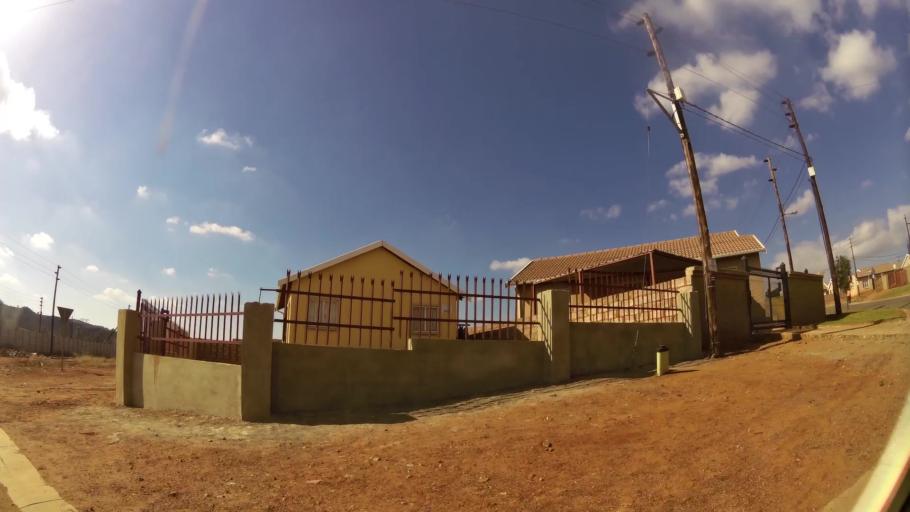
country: ZA
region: Gauteng
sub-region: City of Tshwane Metropolitan Municipality
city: Cullinan
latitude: -25.6866
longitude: 28.4119
